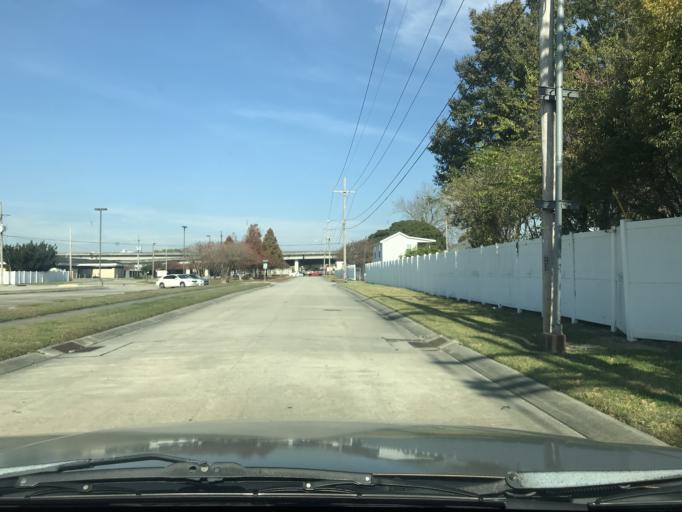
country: US
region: Louisiana
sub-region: Jefferson Parish
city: Marrero
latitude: 29.8932
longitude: -90.0933
